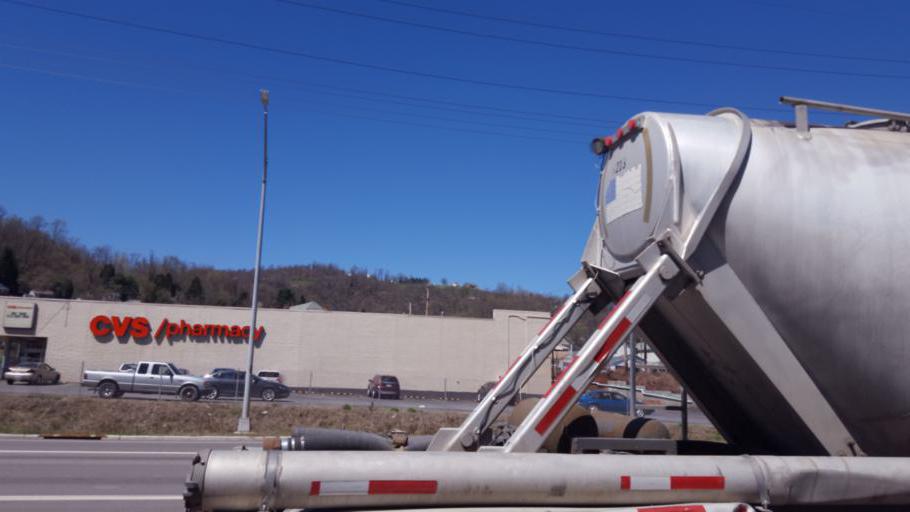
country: US
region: Ohio
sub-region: Belmont County
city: Martins Ferry
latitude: 40.0853
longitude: -80.7342
